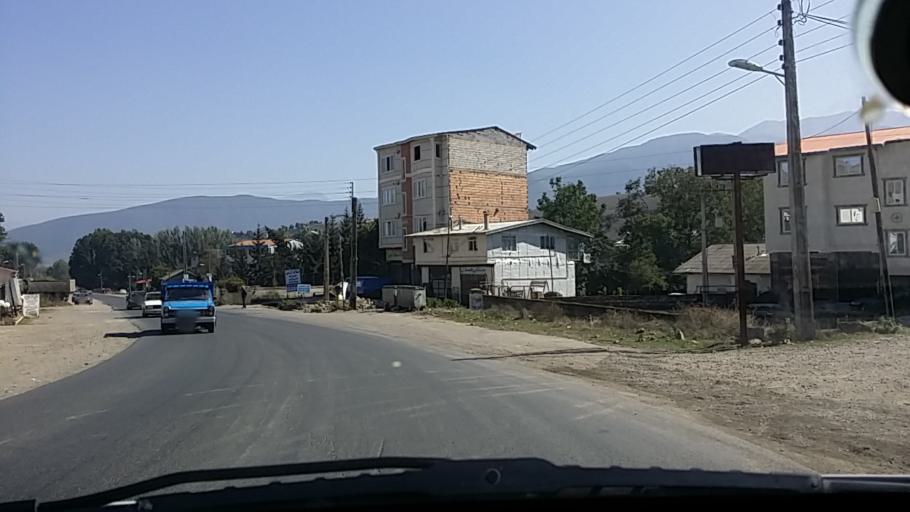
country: IR
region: Mazandaran
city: `Abbasabad
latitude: 36.5465
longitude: 51.1691
